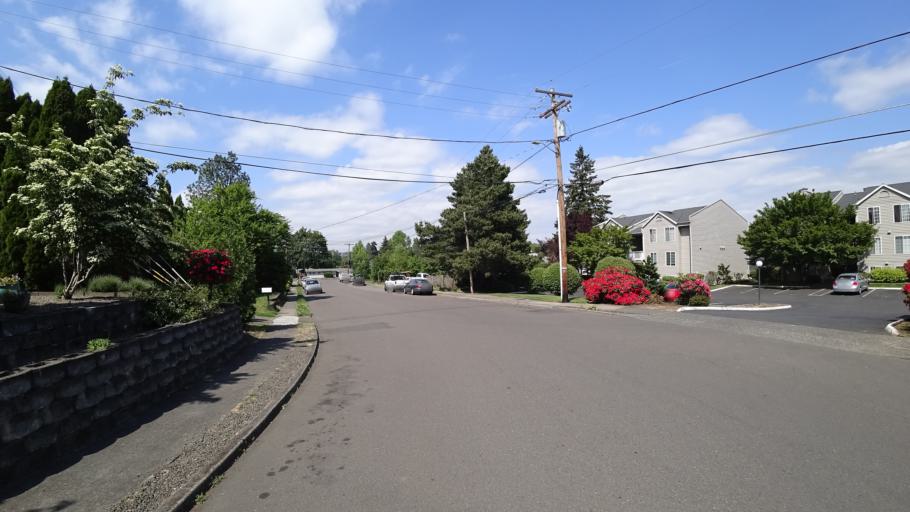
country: US
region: Oregon
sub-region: Washington County
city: Beaverton
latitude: 45.4756
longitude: -122.7953
